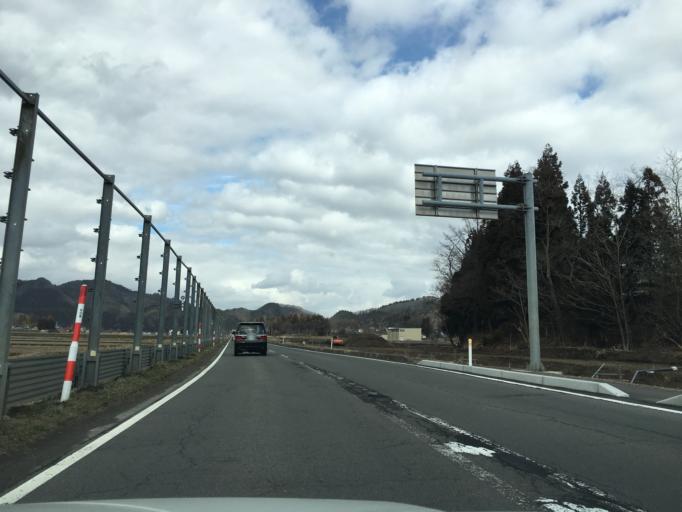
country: JP
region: Akita
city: Hanawa
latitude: 40.2294
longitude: 140.7316
